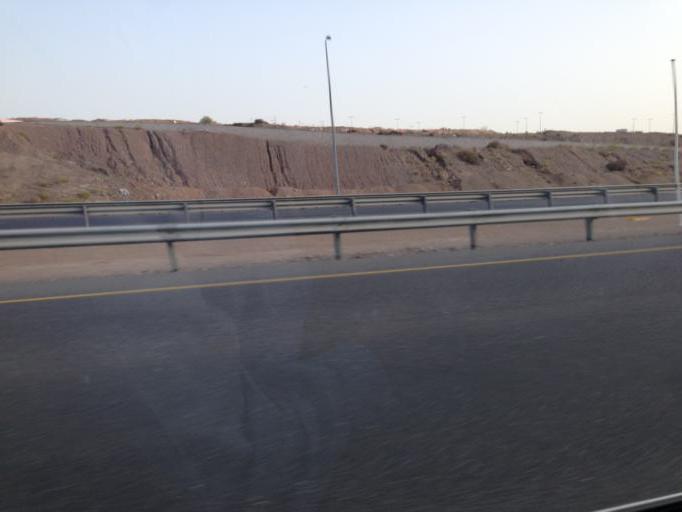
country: OM
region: Muhafazat Masqat
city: Bawshar
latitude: 23.5728
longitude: 58.4287
